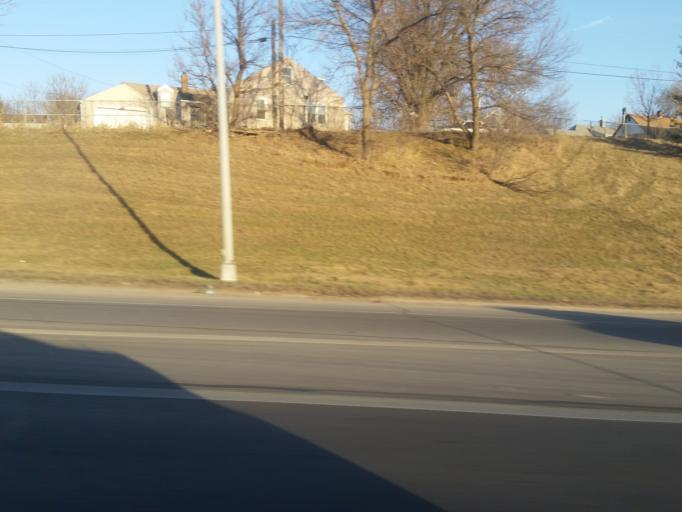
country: US
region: Nebraska
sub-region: Douglas County
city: Omaha
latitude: 41.2213
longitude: -95.9527
